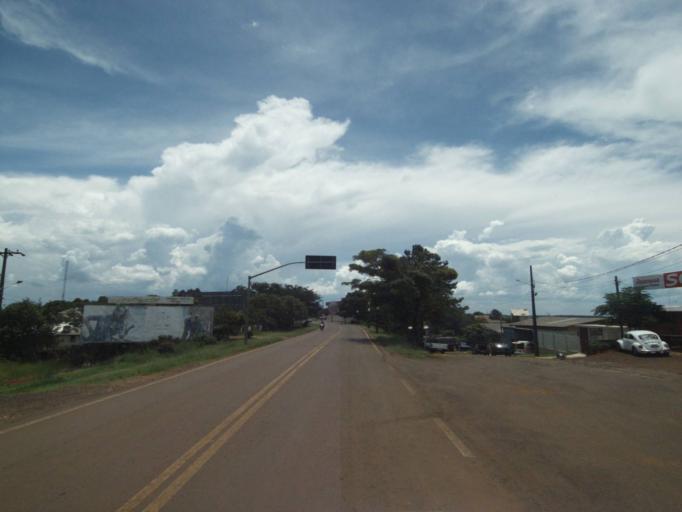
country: BR
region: Parana
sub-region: Guaraniacu
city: Guaraniacu
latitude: -25.0967
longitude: -52.8746
